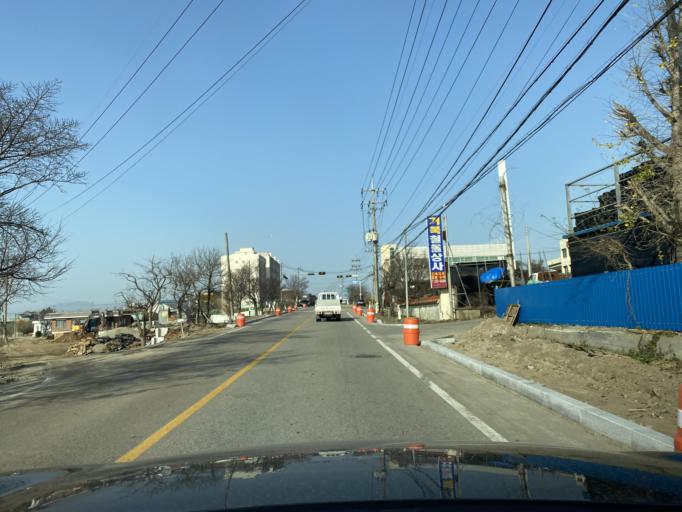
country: KR
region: Chungcheongnam-do
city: Yesan
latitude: 36.6858
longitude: 126.8025
